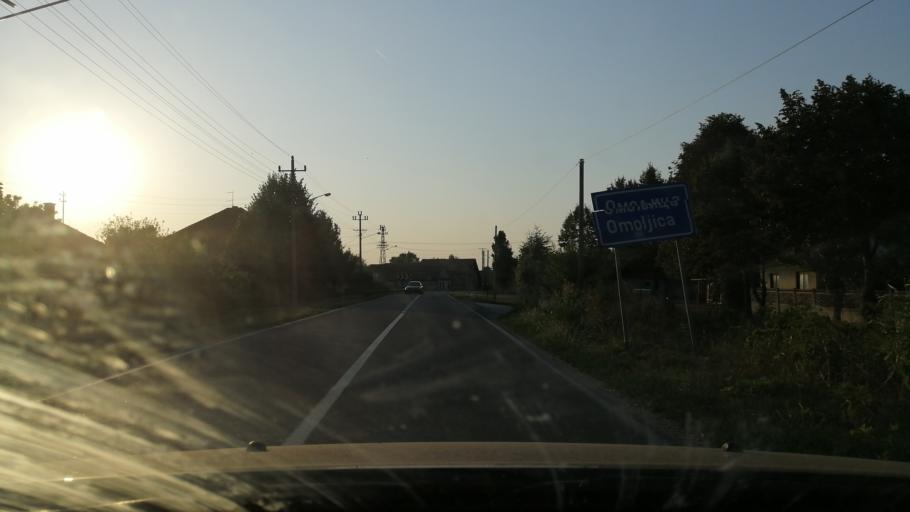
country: RS
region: Central Serbia
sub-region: Belgrade
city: Grocka
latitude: 44.7505
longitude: 20.7506
